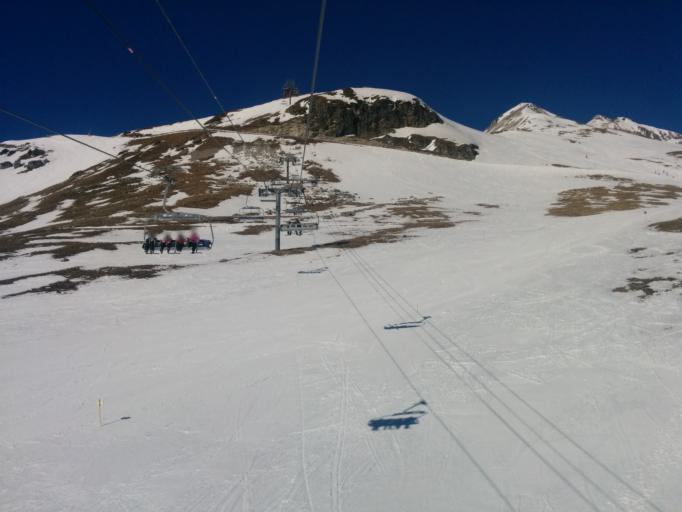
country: FR
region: Rhone-Alpes
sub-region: Departement de la Savoie
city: Modane
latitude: 45.2590
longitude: 6.7369
